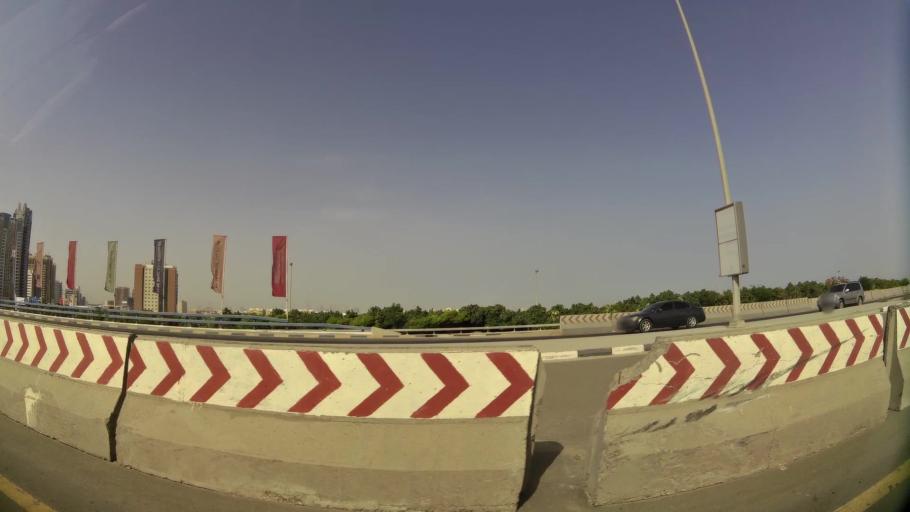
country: AE
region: Ash Shariqah
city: Sharjah
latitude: 25.3024
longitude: 55.3618
